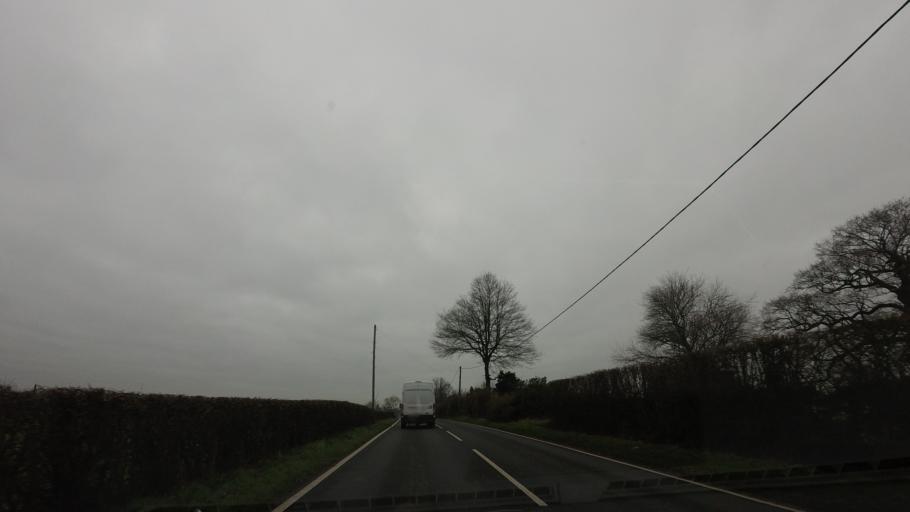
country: GB
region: England
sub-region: Kent
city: Staplehurst
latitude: 51.1485
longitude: 0.5519
